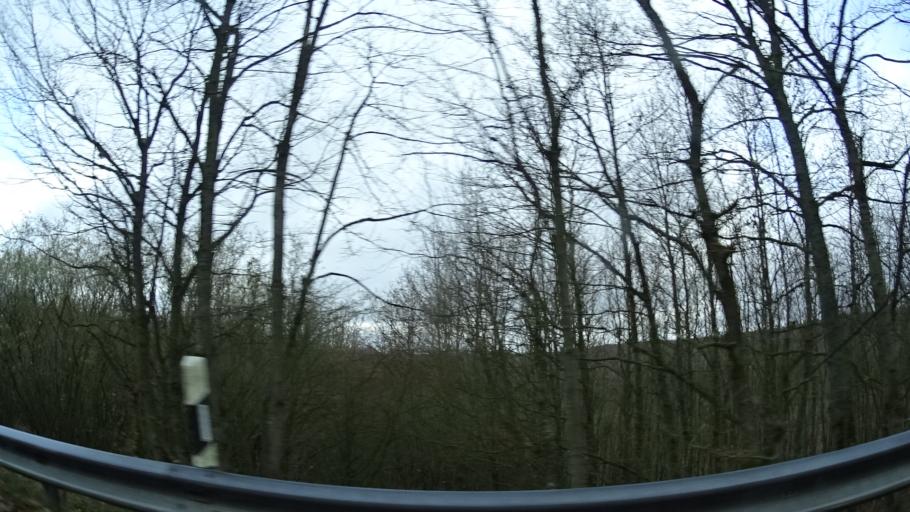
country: DE
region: Rheinland-Pfalz
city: Ruppertsecken
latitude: 49.6806
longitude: 7.9031
